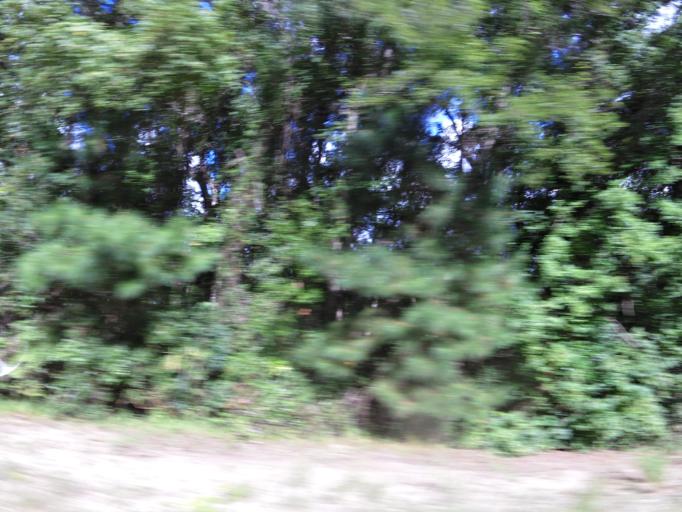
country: US
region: Georgia
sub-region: Camden County
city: Kingsland
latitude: 30.8403
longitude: -81.6982
